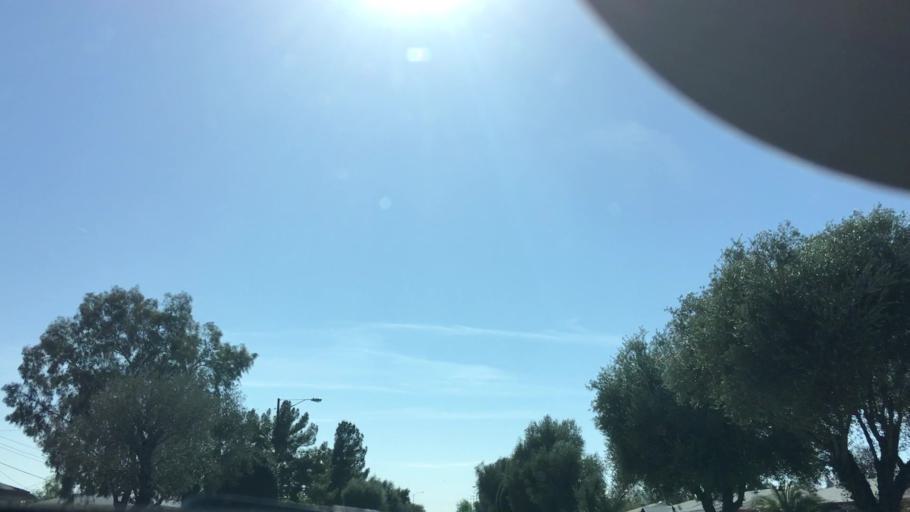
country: US
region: Arizona
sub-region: Maricopa County
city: Phoenix
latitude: 33.4878
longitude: -112.1056
